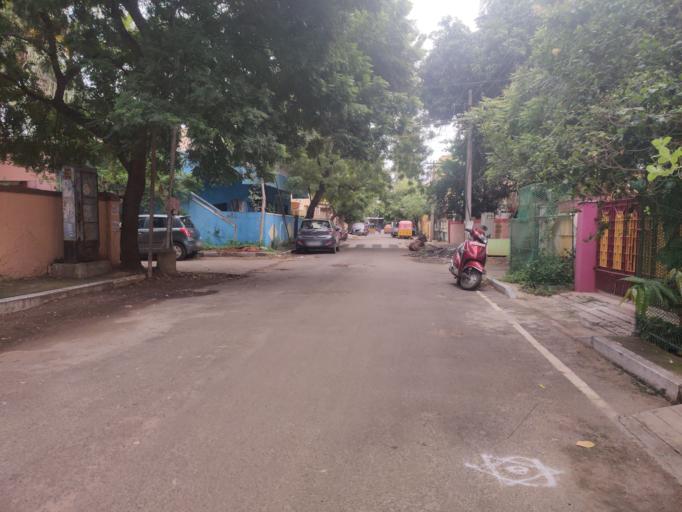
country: IN
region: Tamil Nadu
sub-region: Thiruvallur
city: Chinnasekkadu
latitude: 13.1230
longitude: 80.2194
